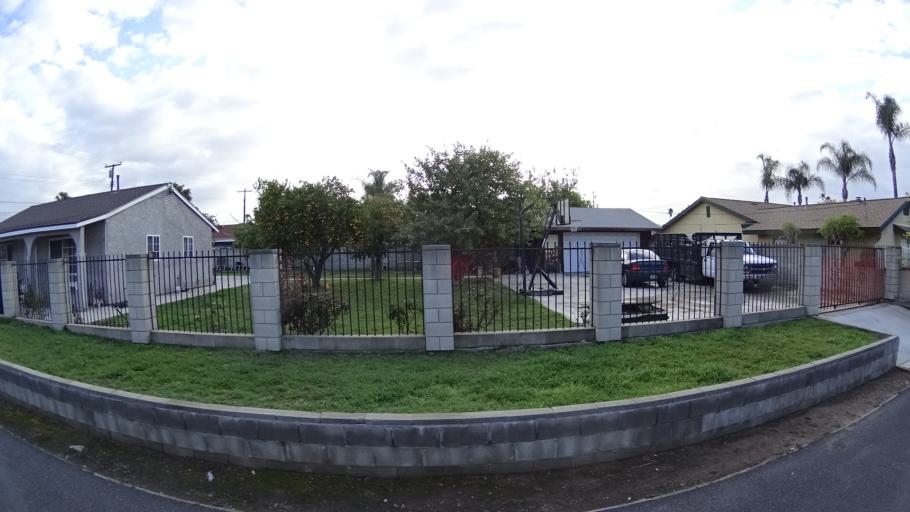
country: US
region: California
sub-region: Los Angeles County
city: Baldwin Park
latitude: 34.0946
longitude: -117.9746
